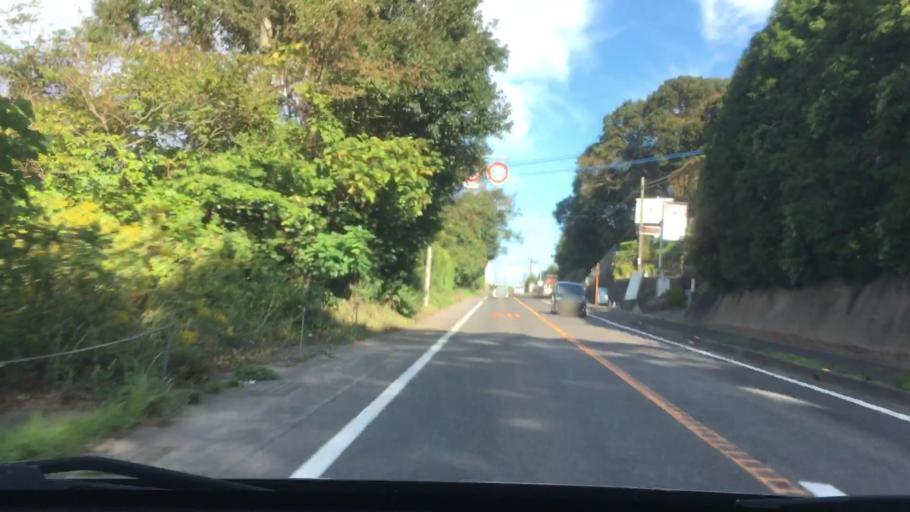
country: JP
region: Nagasaki
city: Sasebo
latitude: 33.0691
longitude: 129.7632
